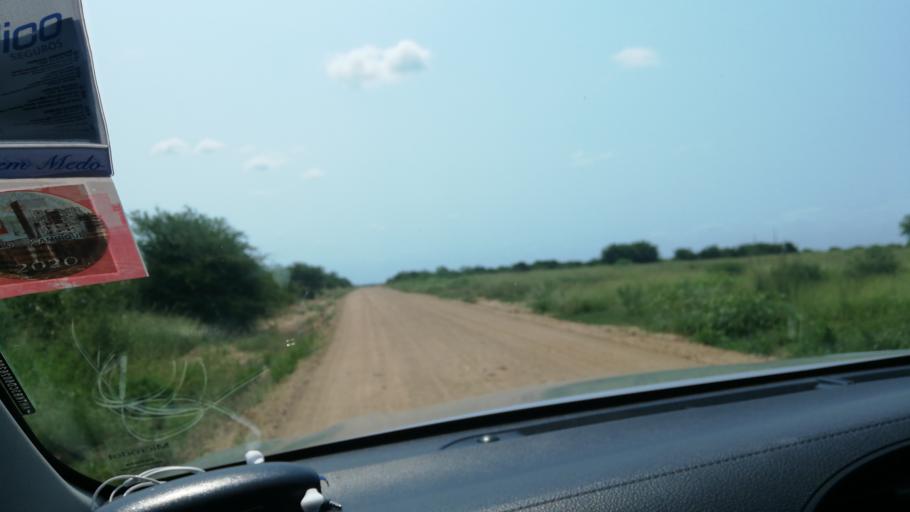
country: MZ
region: Maputo
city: Matola
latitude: -26.0855
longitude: 32.3915
